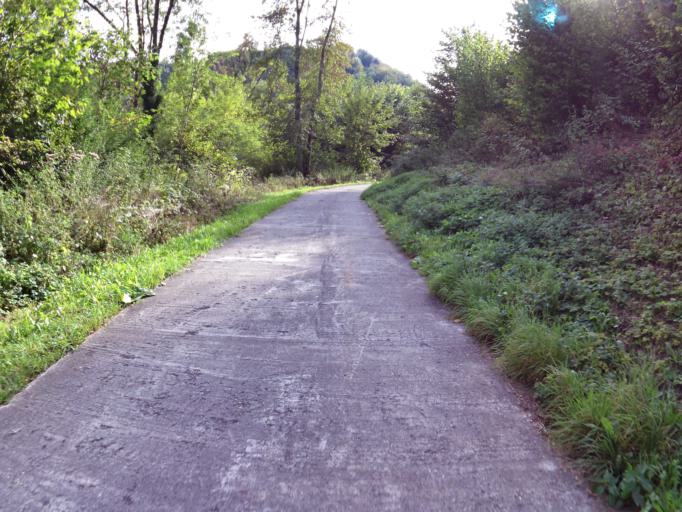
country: DE
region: Baden-Wuerttemberg
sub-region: Freiburg Region
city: Villingendorf
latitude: 48.2083
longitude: 8.6074
